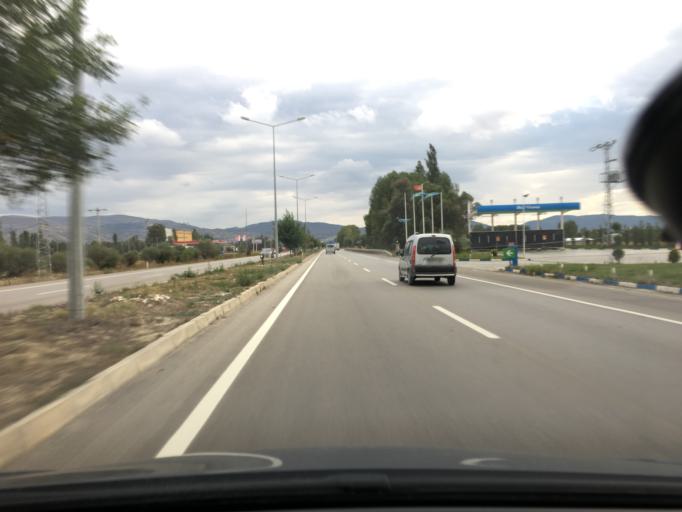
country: TR
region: Afyonkarahisar
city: Sincanli
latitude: 38.7600
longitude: 30.3630
